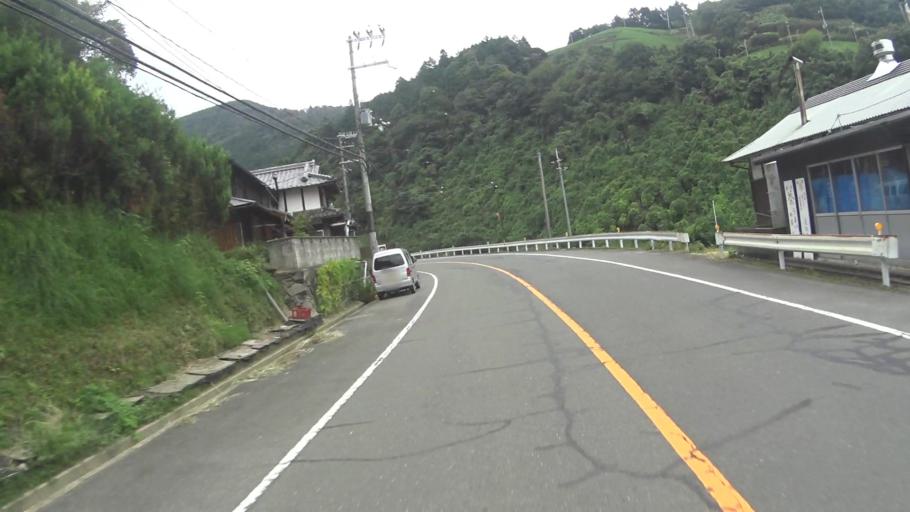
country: JP
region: Kyoto
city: Uji
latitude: 34.8127
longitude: 135.9200
